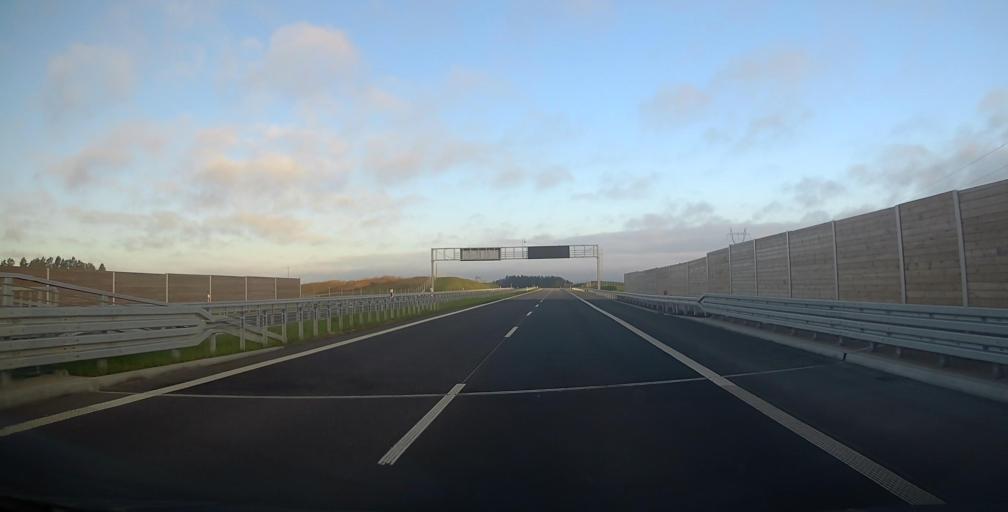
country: PL
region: Podlasie
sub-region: Powiat grajewski
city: Szczuczyn
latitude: 53.6799
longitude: 22.2956
